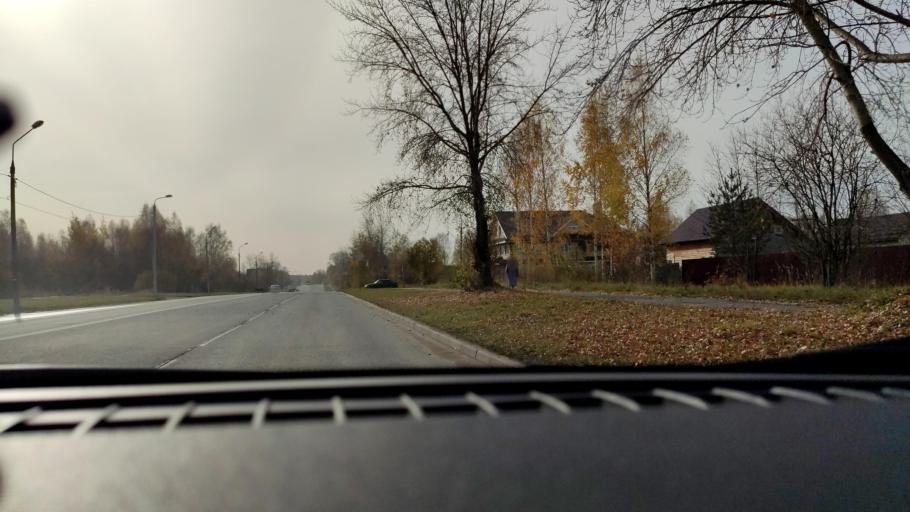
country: RU
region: Perm
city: Polazna
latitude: 58.1275
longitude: 56.4062
